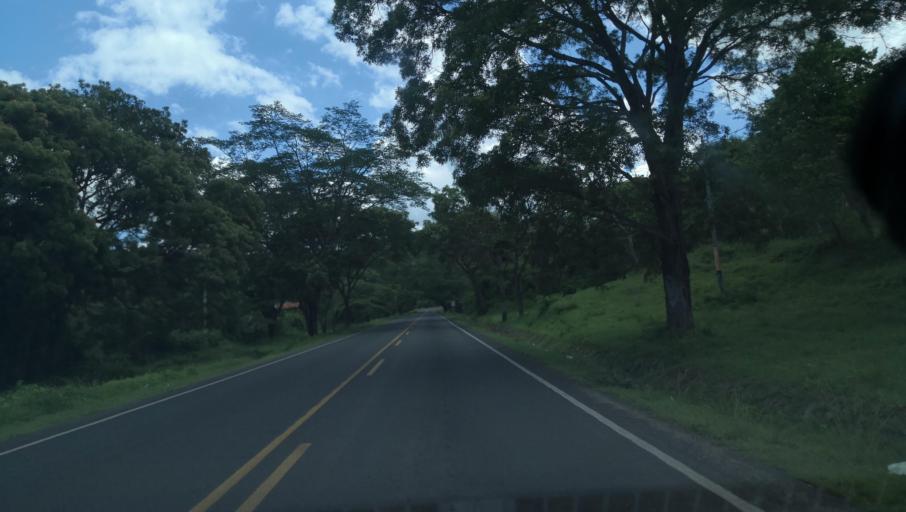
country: NI
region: Madriz
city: Palacaguina
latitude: 13.4342
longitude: -86.4214
